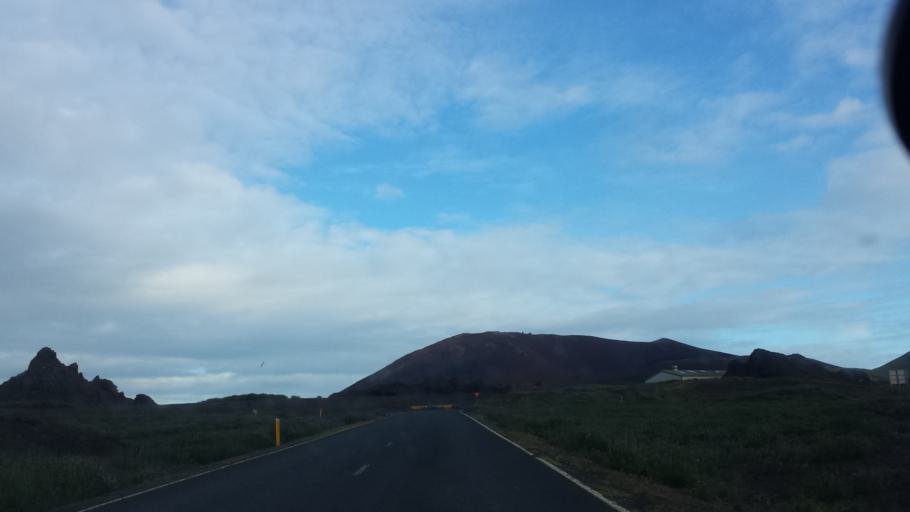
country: IS
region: South
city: Vestmannaeyjar
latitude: 63.4421
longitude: -20.2554
